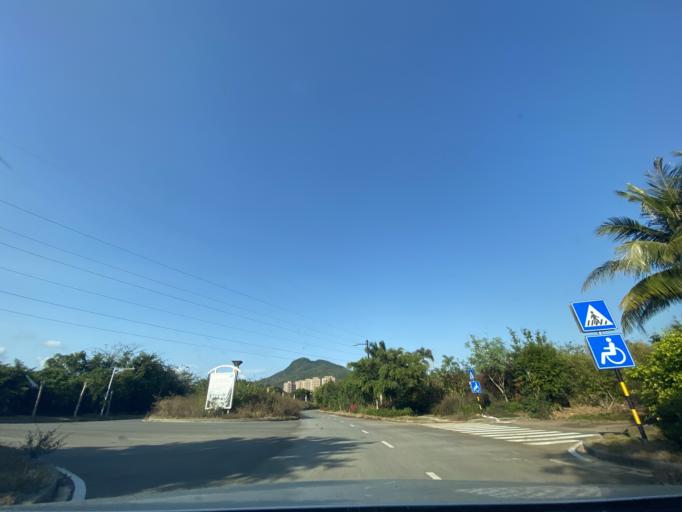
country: CN
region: Hainan
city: Yingzhou
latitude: 18.4486
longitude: 109.8508
